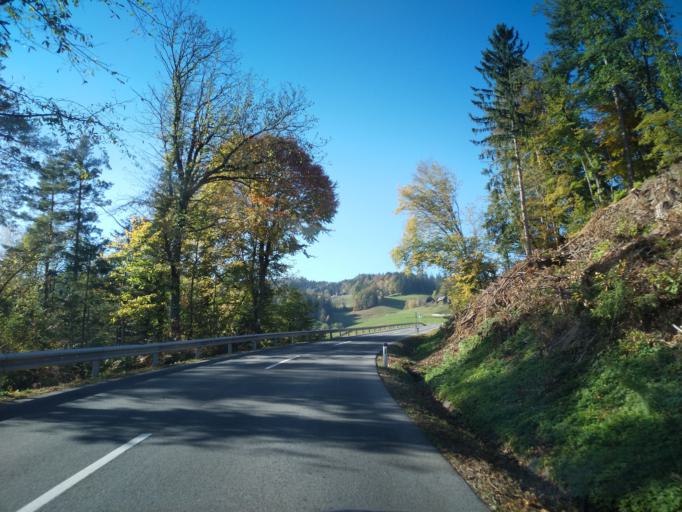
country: AT
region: Styria
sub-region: Politischer Bezirk Deutschlandsberg
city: Hollenegg
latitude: 46.8051
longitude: 15.1982
